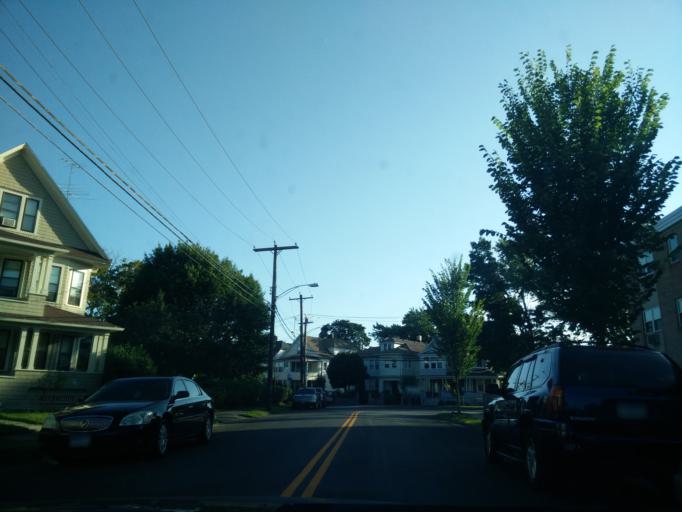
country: US
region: Connecticut
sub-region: Fairfield County
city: Bridgeport
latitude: 41.1599
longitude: -73.2224
